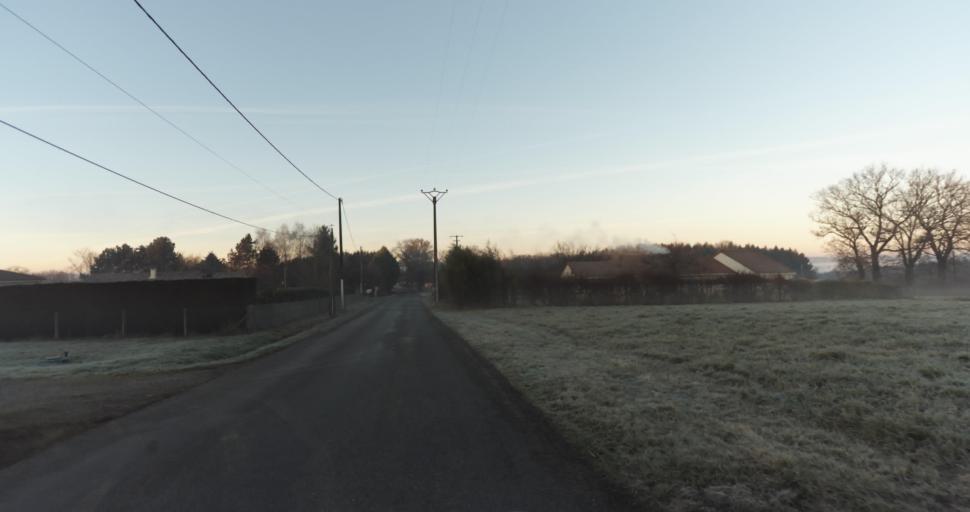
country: FR
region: Limousin
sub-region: Departement de la Haute-Vienne
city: Aixe-sur-Vienne
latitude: 45.8159
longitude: 1.1434
